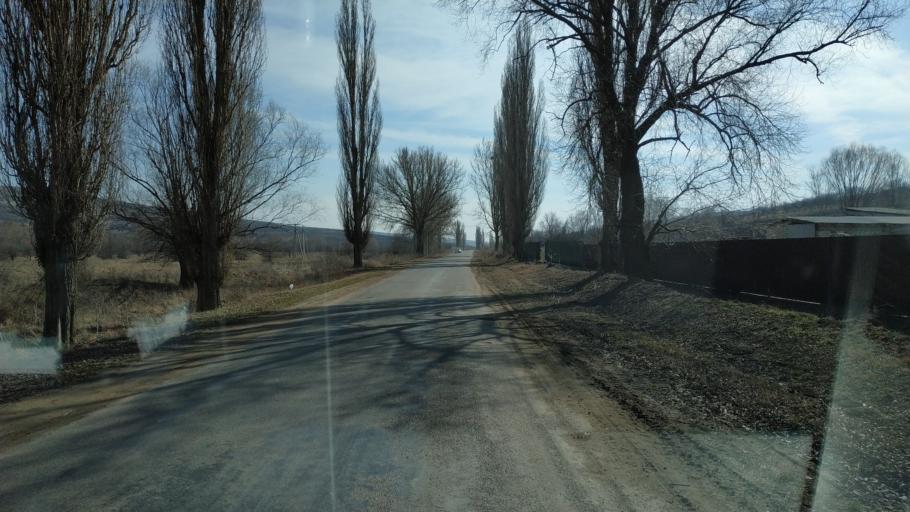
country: MD
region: Nisporeni
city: Nisporeni
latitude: 47.1605
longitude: 28.1041
